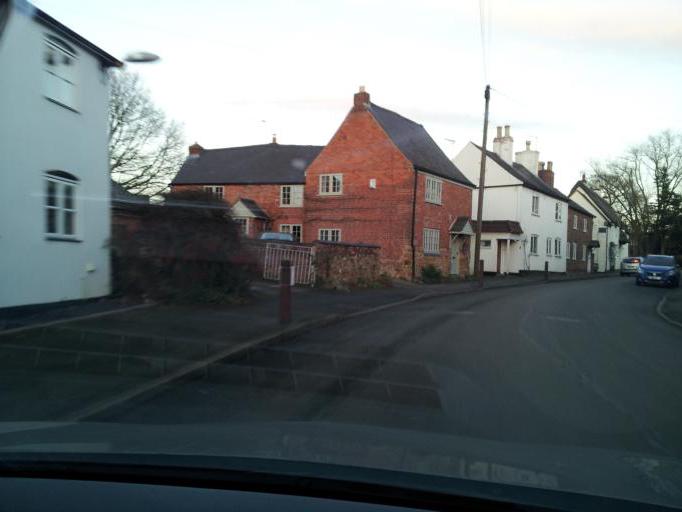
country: GB
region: England
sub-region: Leicestershire
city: Houghton on the Hill
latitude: 52.6242
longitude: -1.0010
